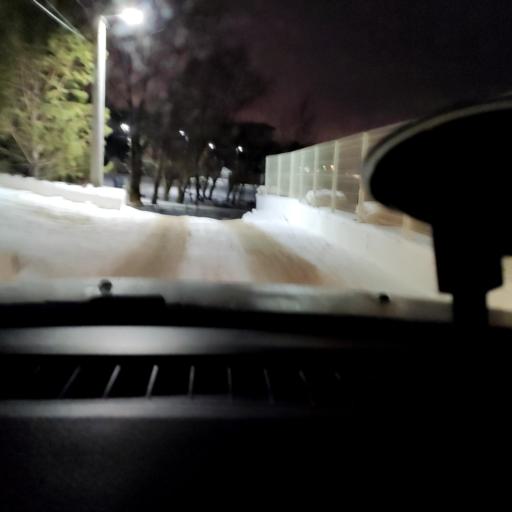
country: RU
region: Samara
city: Samara
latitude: 53.2819
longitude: 50.1891
